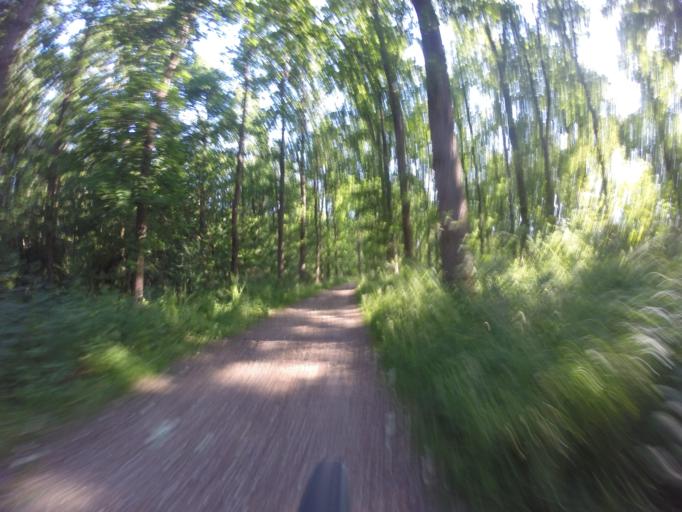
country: DK
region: Capital Region
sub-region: Ballerup Kommune
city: Ballerup
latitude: 55.6995
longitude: 12.3395
